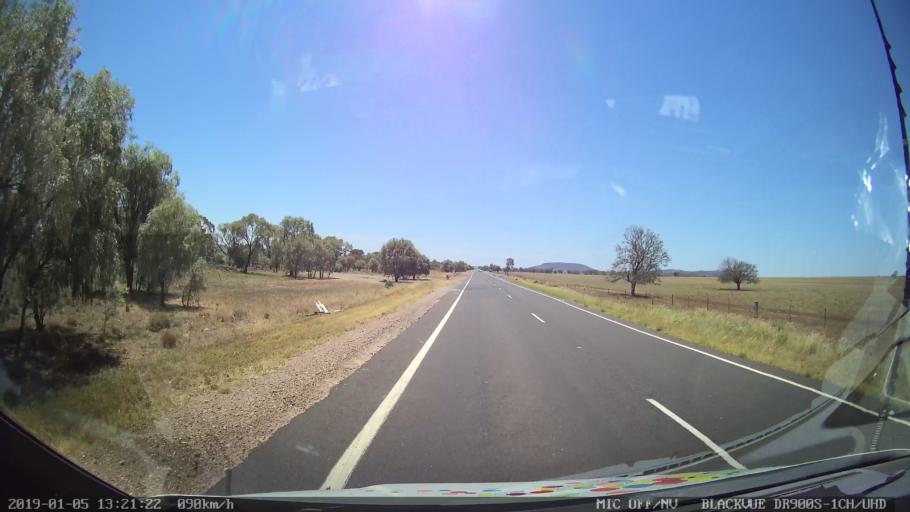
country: AU
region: New South Wales
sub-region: Gunnedah
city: Gunnedah
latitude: -31.0950
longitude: 149.9477
